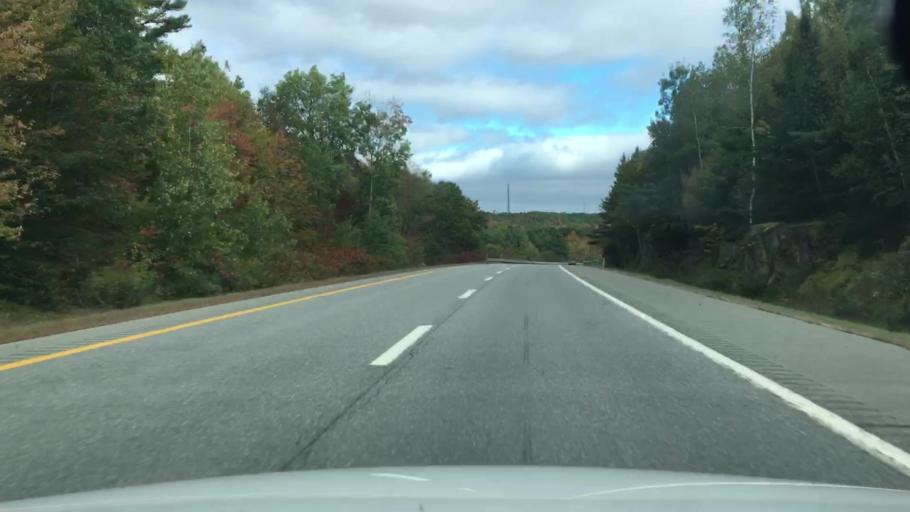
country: US
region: Maine
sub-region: Penobscot County
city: Carmel
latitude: 44.7721
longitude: -69.0079
